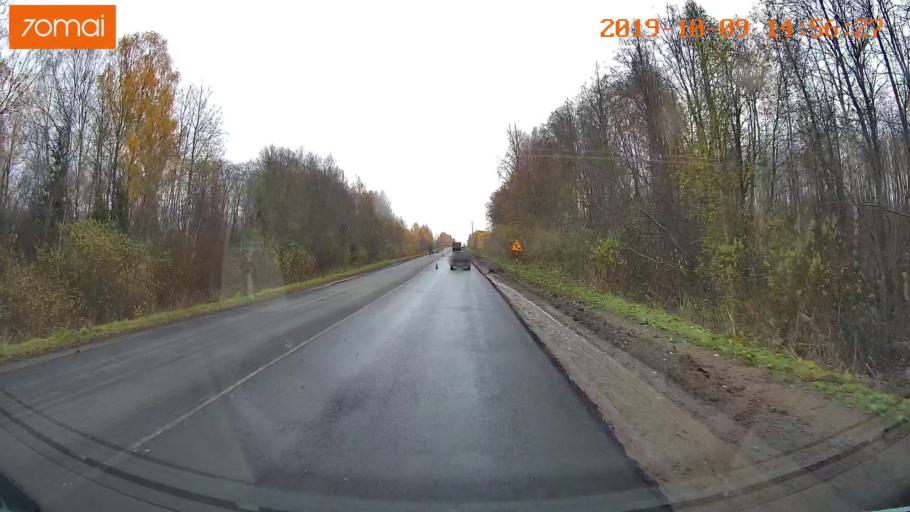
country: RU
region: Kostroma
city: Chistyye Bory
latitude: 58.3457
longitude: 41.6474
